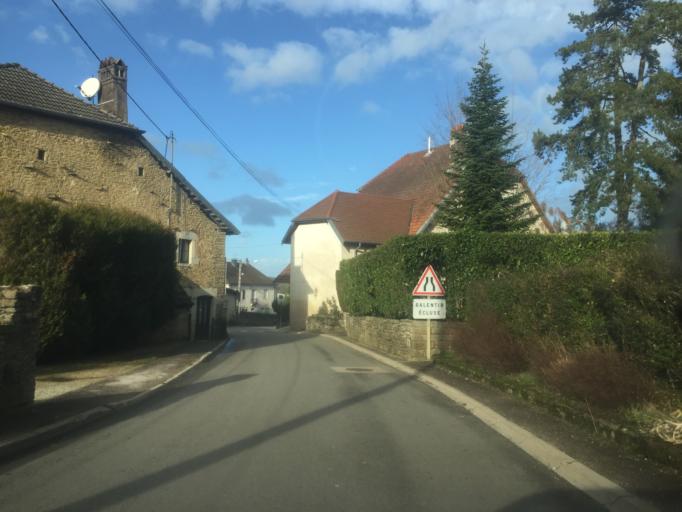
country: FR
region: Franche-Comte
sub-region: Departement du Doubs
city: Saint-Vit
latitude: 47.2039
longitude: 5.8030
